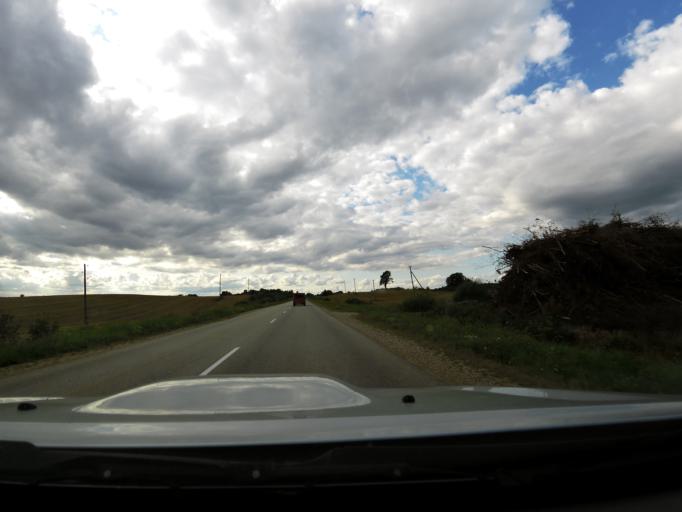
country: LV
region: Ilukste
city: Ilukste
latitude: 55.9736
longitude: 26.0223
